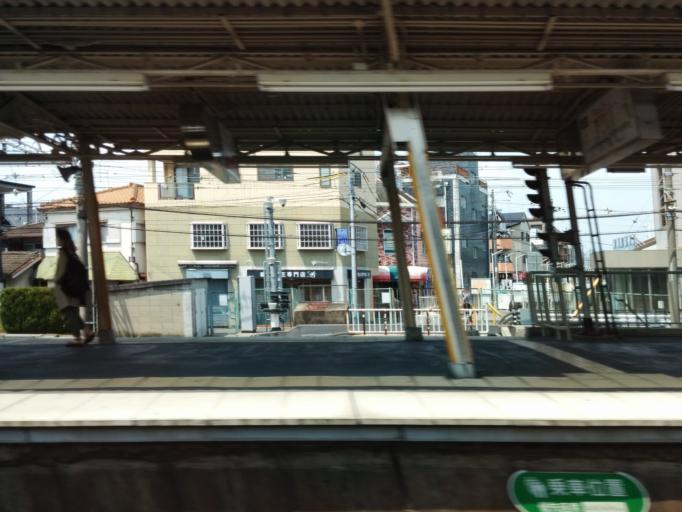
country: JP
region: Osaka
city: Suita
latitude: 34.7759
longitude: 135.5460
